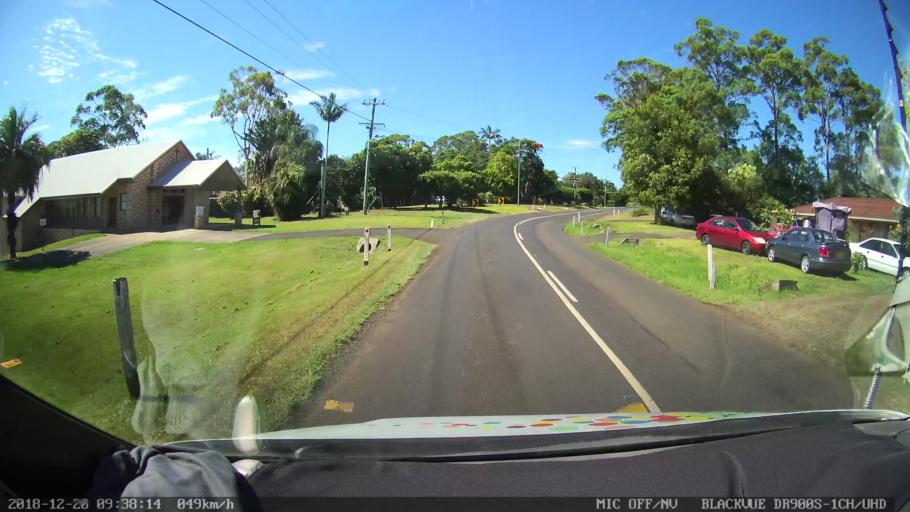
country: AU
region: New South Wales
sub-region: Lismore Municipality
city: Goonellabah
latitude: -28.6891
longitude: 153.3144
